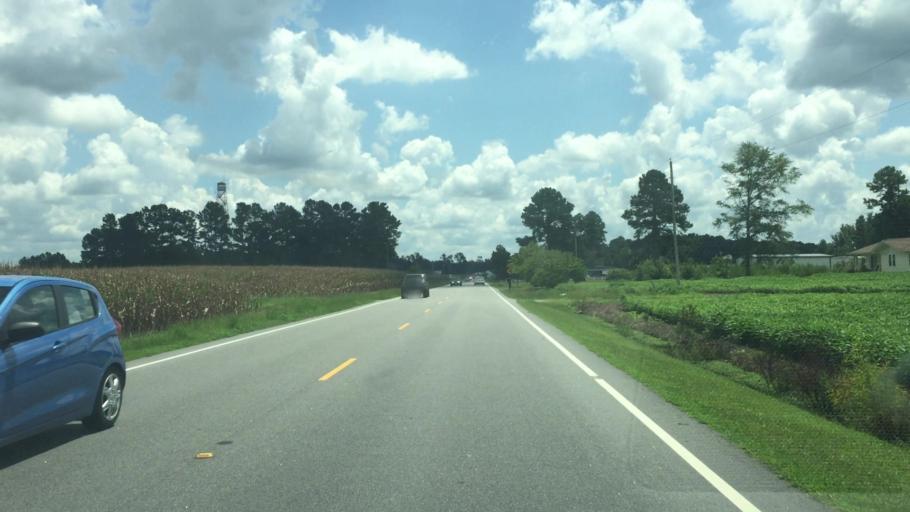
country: US
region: North Carolina
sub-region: Columbus County
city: Chadbourn
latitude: 34.2811
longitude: -78.8175
